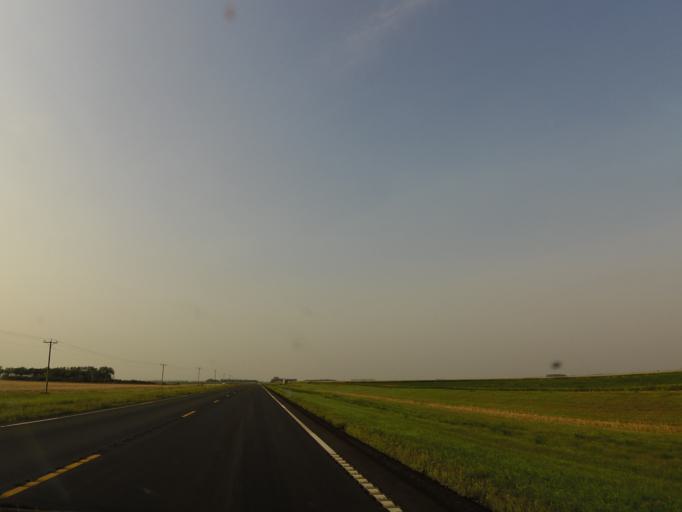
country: US
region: North Dakota
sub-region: Traill County
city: Mayville
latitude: 47.3710
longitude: -97.3262
